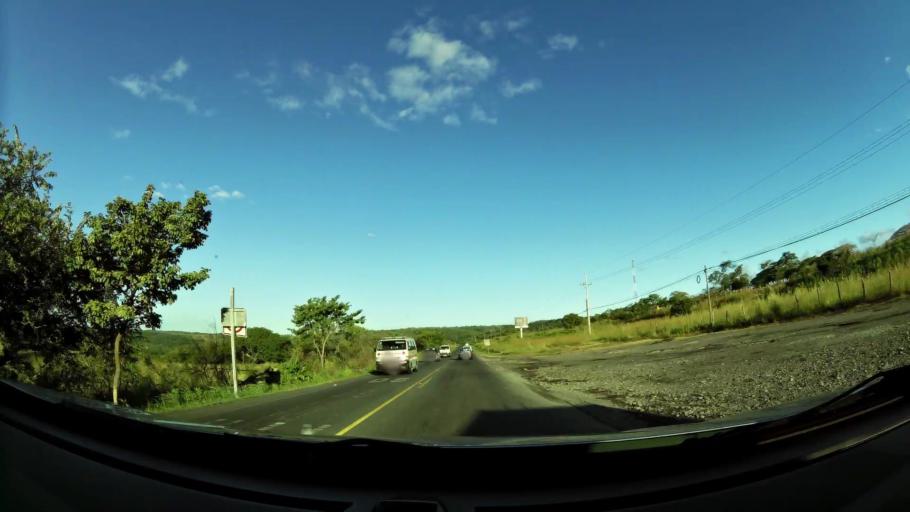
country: CR
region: Puntarenas
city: Miramar
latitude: 10.0955
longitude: -84.8003
